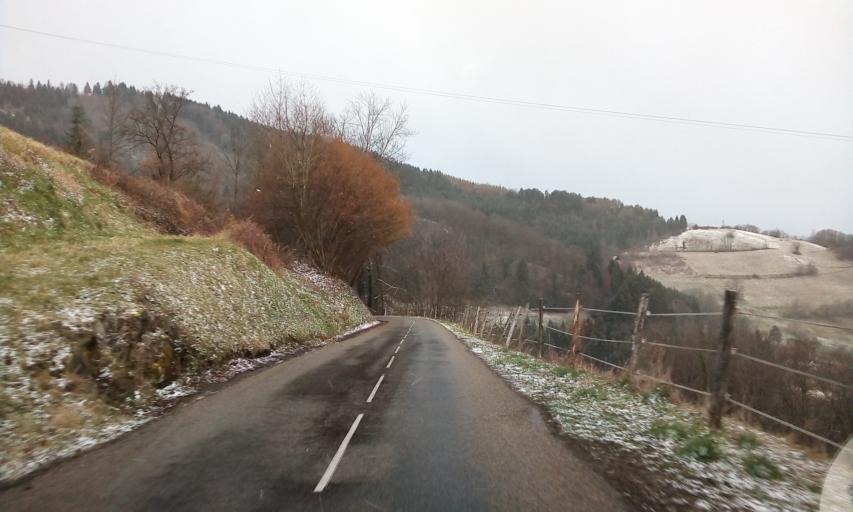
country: FR
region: Rhone-Alpes
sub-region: Departement de l'Isere
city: Revel
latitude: 45.2062
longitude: 5.8819
